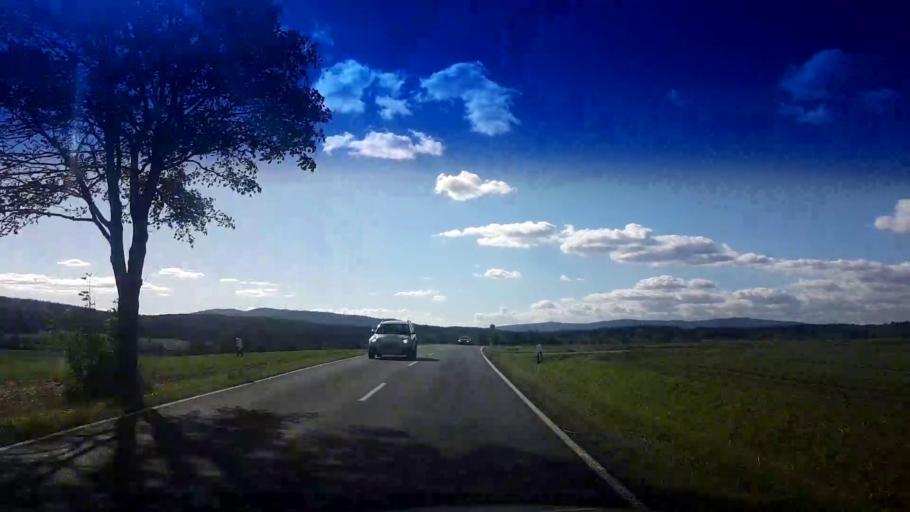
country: DE
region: Bavaria
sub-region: Upper Franconia
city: Marktredwitz
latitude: 50.0343
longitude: 12.0895
